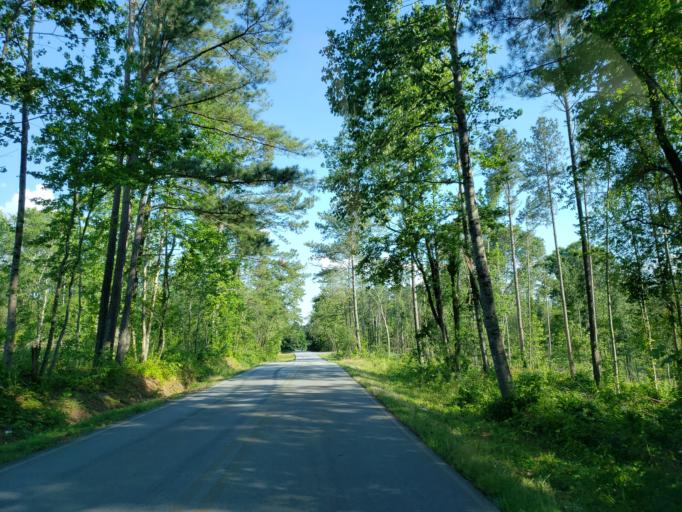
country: US
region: Georgia
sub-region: Haralson County
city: Bremen
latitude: 33.6947
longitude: -85.0988
